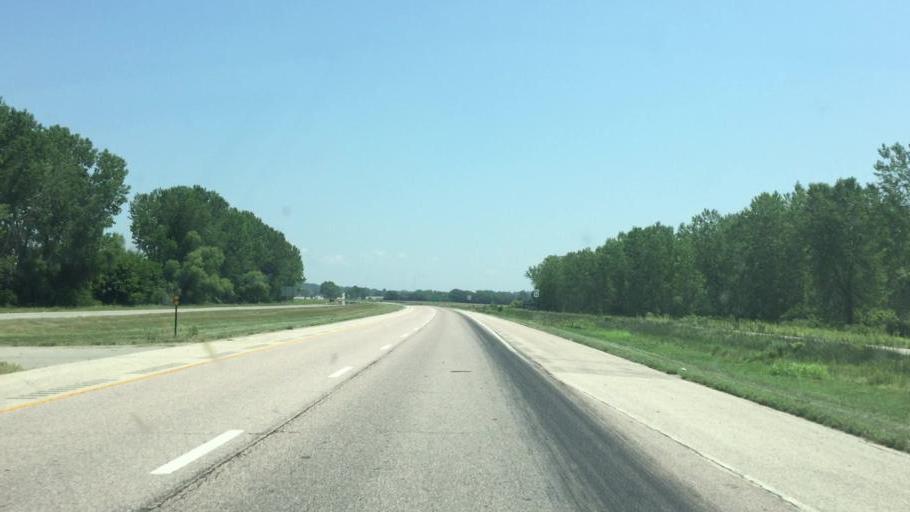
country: US
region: Kansas
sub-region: Doniphan County
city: Elwood
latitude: 39.7421
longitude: -94.8878
